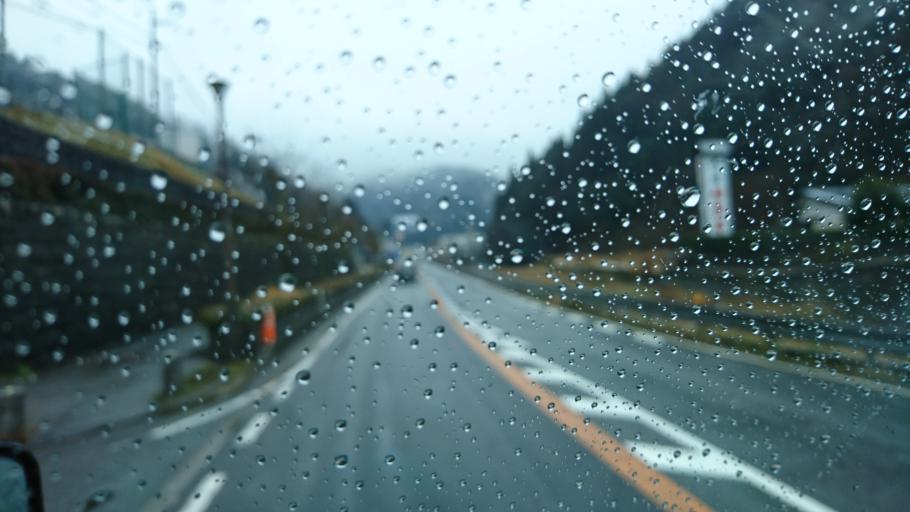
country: JP
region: Tottori
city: Tottori
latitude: 35.5613
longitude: 134.4835
